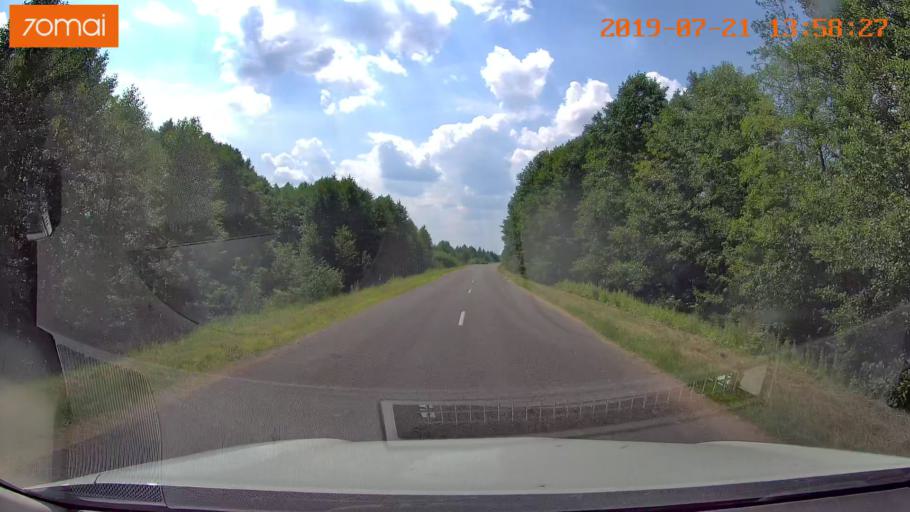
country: BY
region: Grodnenskaya
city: Lyubcha
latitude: 53.7611
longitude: 26.0797
